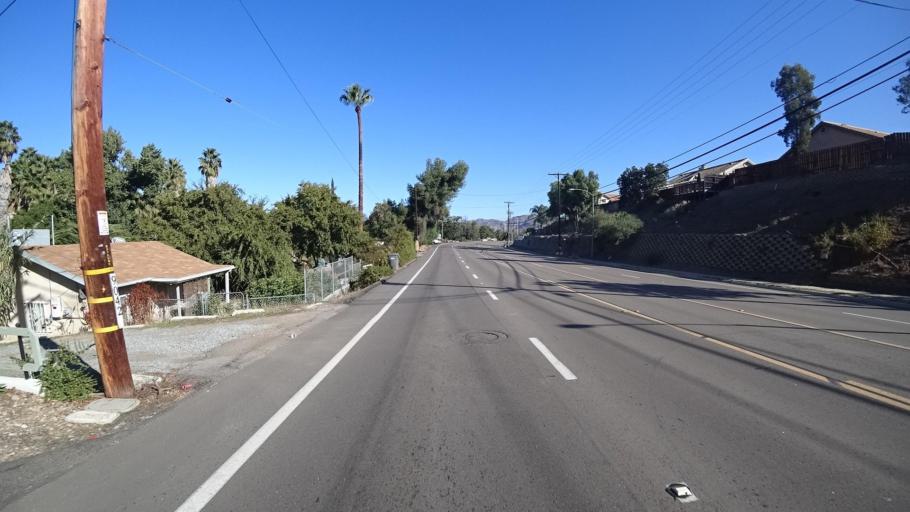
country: US
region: California
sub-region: San Diego County
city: Winter Gardens
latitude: 32.8417
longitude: -116.9331
